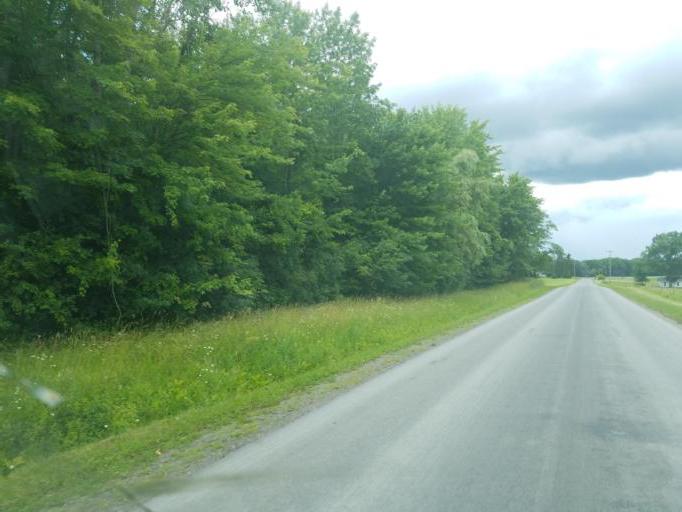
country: US
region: New York
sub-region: Wayne County
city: Clyde
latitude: 43.0493
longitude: -76.8840
